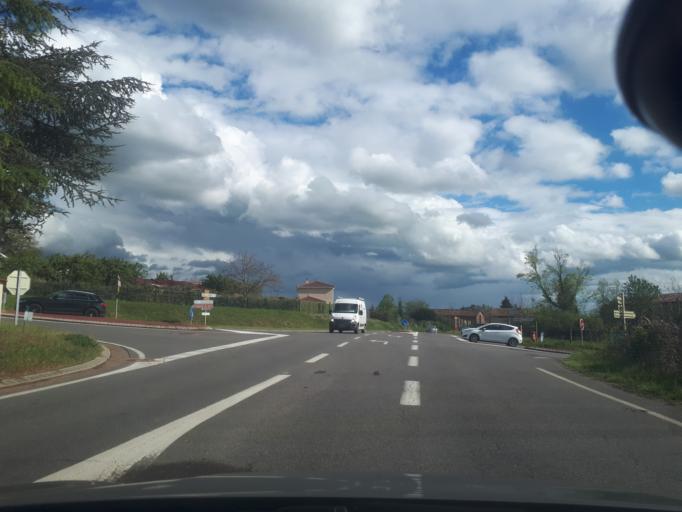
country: FR
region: Rhone-Alpes
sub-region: Departement de la Loire
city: Civens
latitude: 45.7622
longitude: 4.2679
